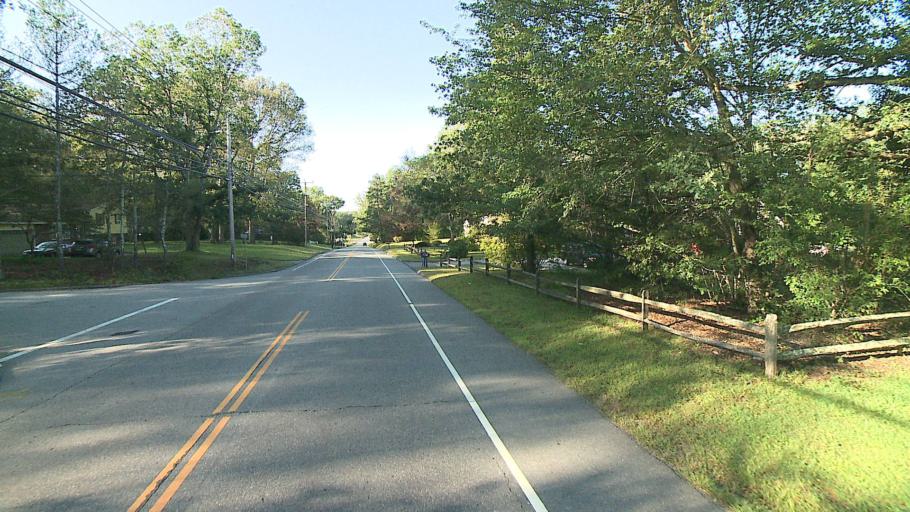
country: US
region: Connecticut
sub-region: Windham County
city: East Brooklyn
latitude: 41.7718
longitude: -71.8975
